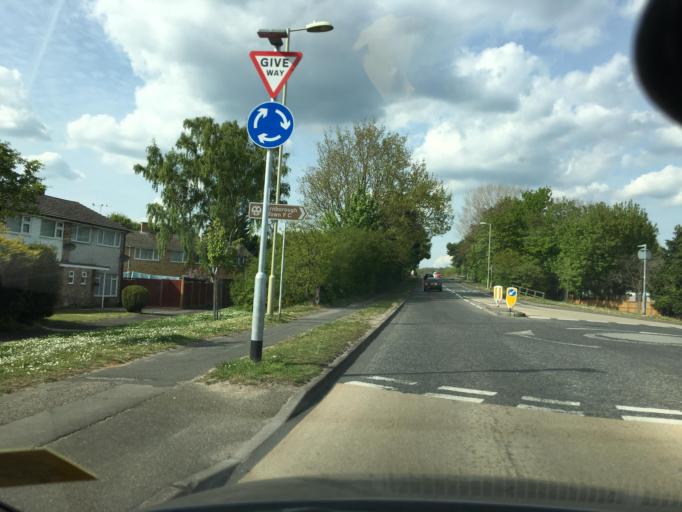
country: GB
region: England
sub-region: Hampshire
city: Farnborough
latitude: 51.3071
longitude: -0.7750
